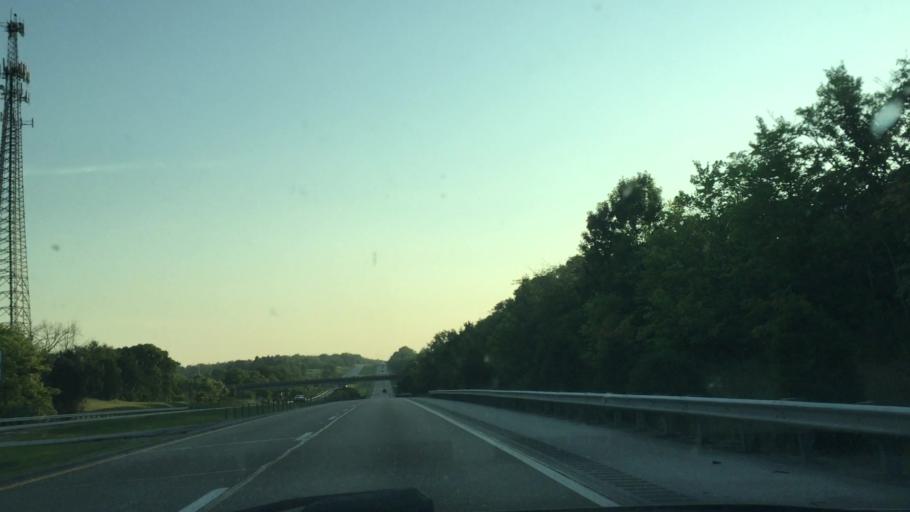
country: US
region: Indiana
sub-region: Switzerland County
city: Vevay
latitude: 38.6622
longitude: -85.0360
